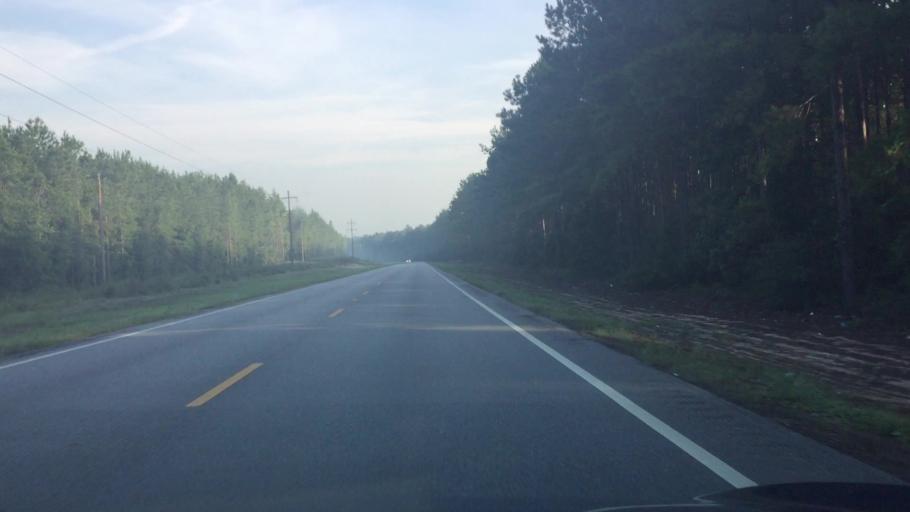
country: US
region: Alabama
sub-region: Covington County
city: Florala
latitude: 31.0537
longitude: -86.3897
